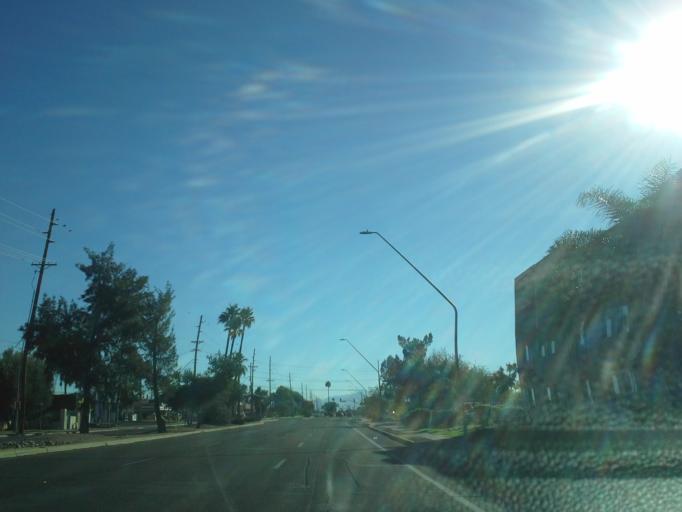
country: US
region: Arizona
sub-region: Pima County
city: Drexel Heights
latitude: 32.1339
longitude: -110.9709
